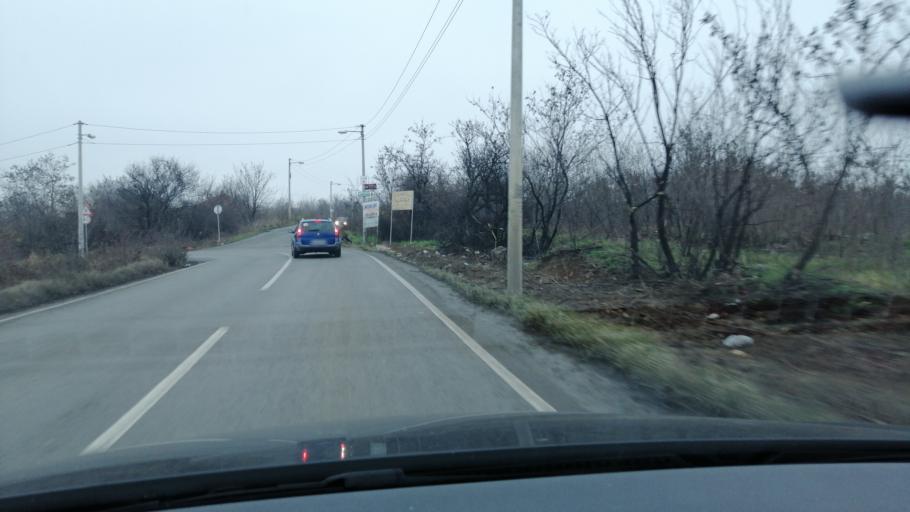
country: RS
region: Central Serbia
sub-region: Belgrade
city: Zvezdara
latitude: 44.7840
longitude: 20.5487
